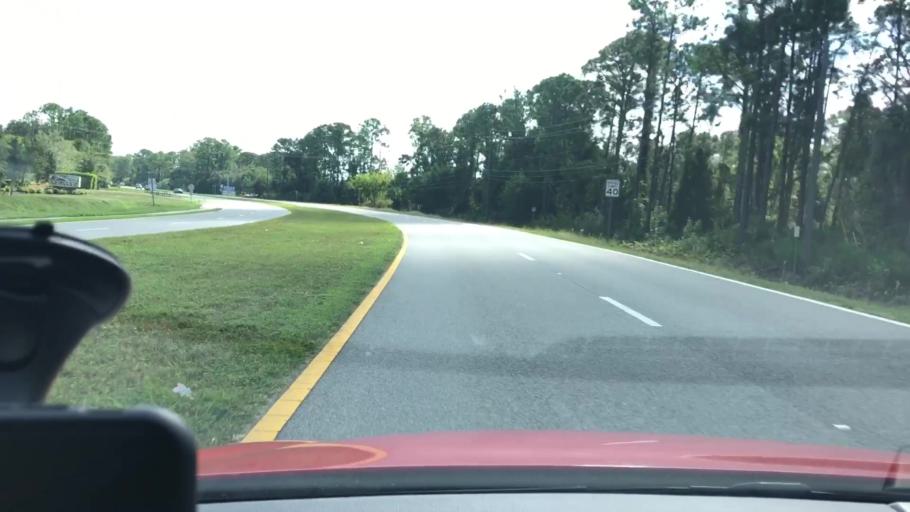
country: US
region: Florida
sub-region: Volusia County
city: Holly Hill
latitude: 29.2083
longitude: -81.0743
